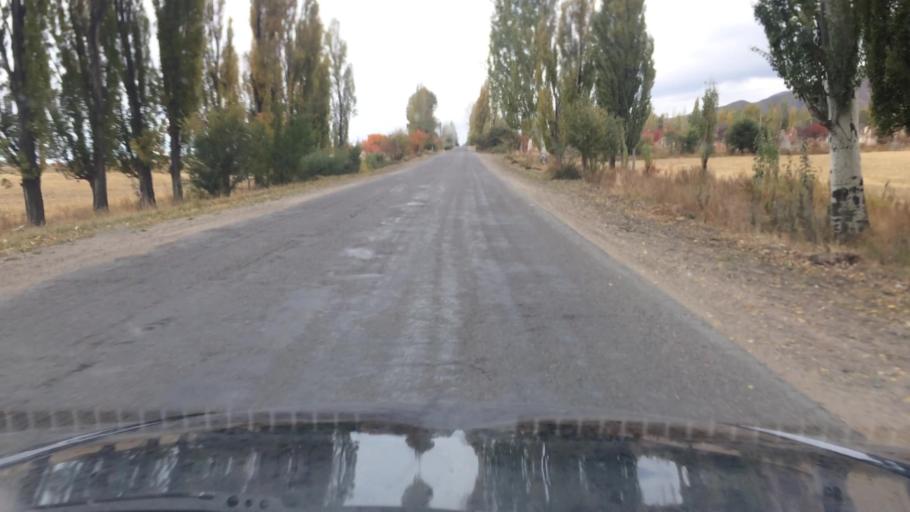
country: KG
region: Ysyk-Koel
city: Pokrovka
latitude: 42.7364
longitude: 77.9562
